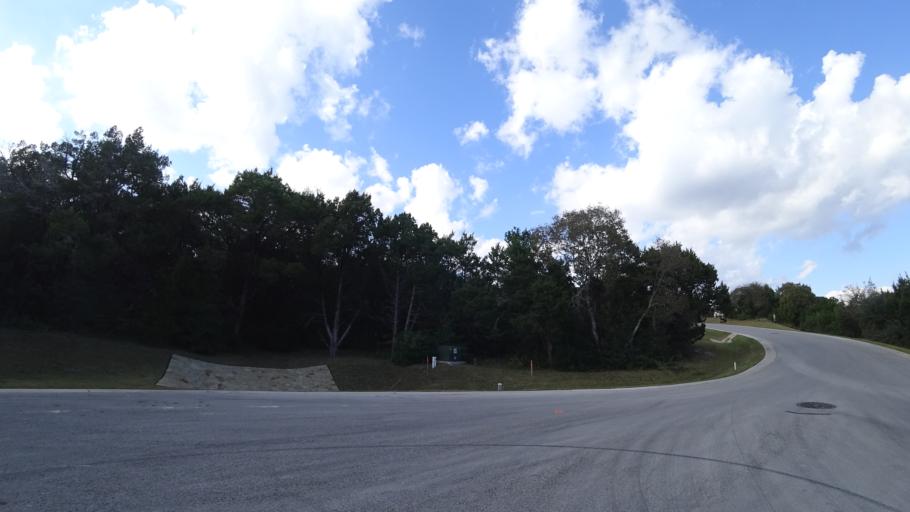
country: US
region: Texas
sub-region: Travis County
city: Barton Creek
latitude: 30.2667
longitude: -97.8803
